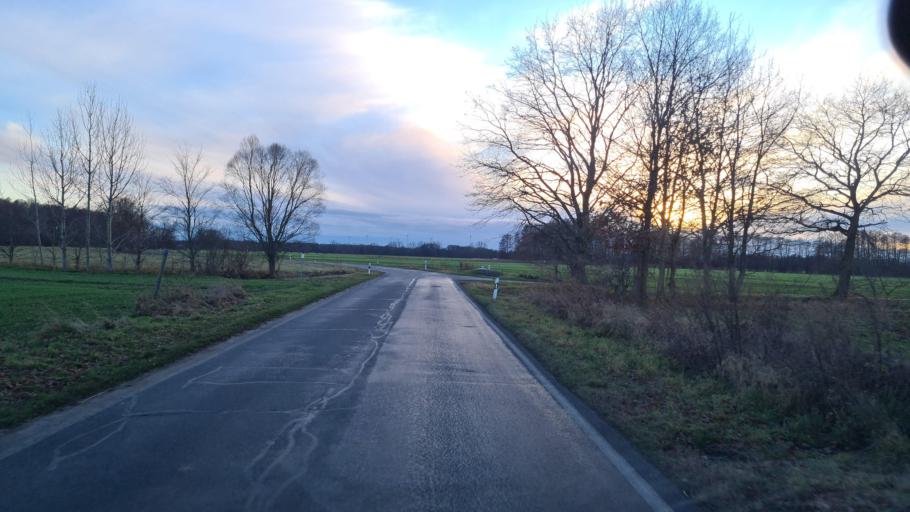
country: DE
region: Brandenburg
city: Burg
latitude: 51.8055
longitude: 14.1381
